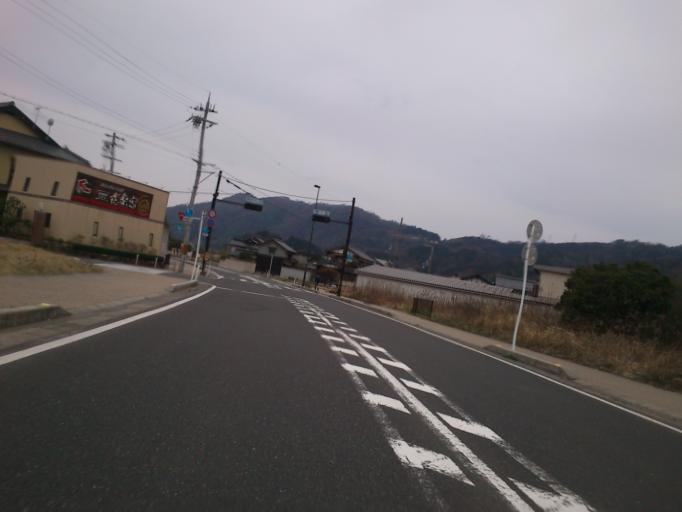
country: JP
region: Kyoto
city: Miyazu
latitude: 35.5698
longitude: 135.1596
